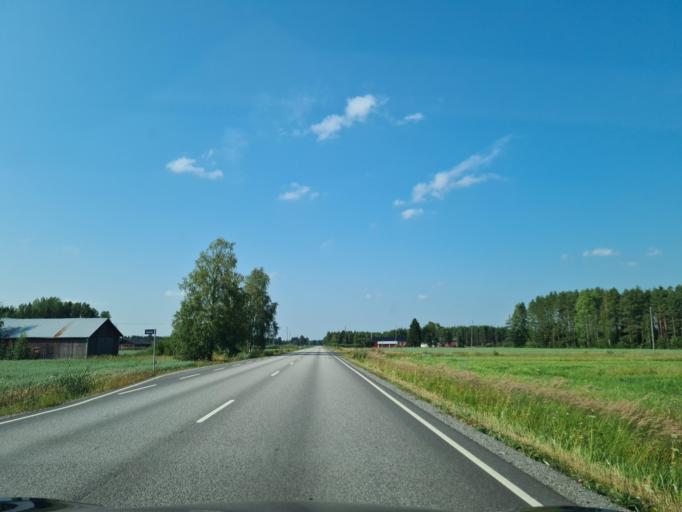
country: FI
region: Satakunta
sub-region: Pohjois-Satakunta
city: Karvia
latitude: 62.0440
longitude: 22.5143
